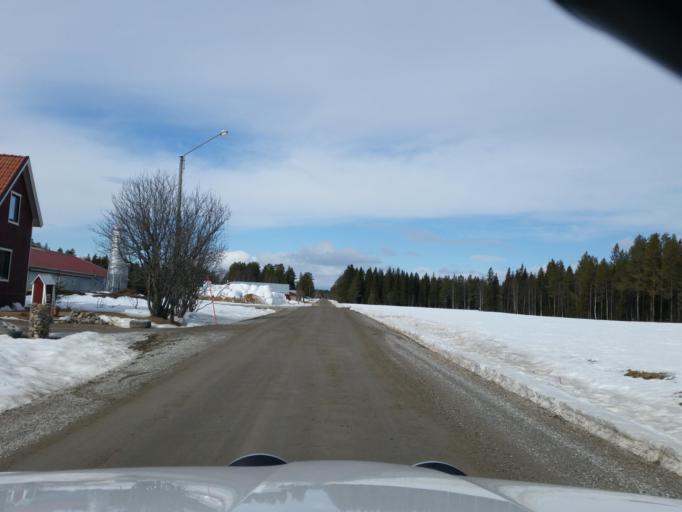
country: SE
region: Vaesterbotten
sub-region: Skelleftea Kommun
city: Storvik
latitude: 65.2048
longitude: 20.9648
